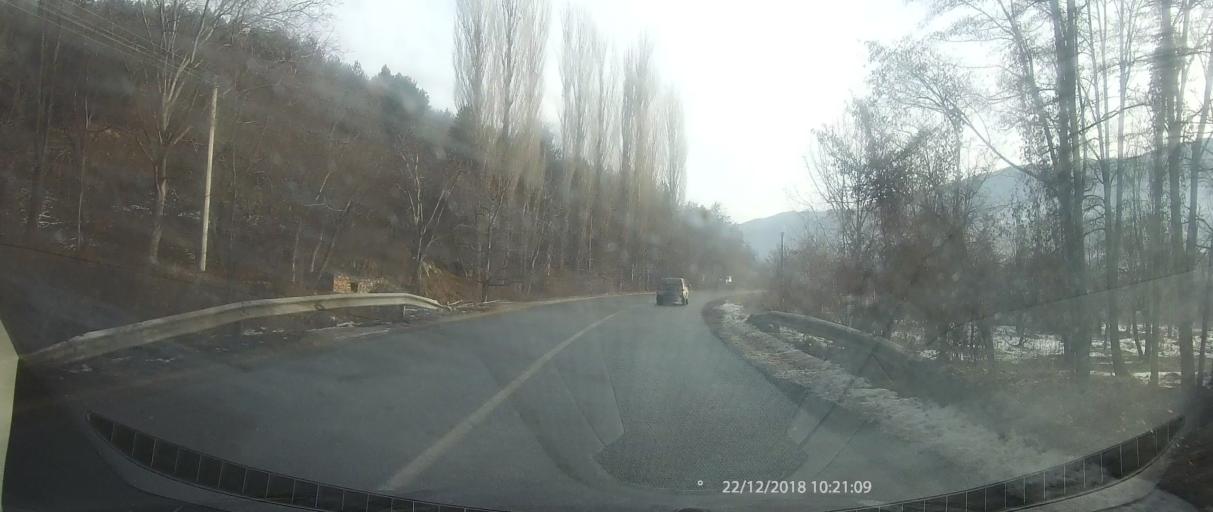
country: MK
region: Kriva Palanka
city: Kriva Palanka
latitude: 42.1971
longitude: 22.3122
